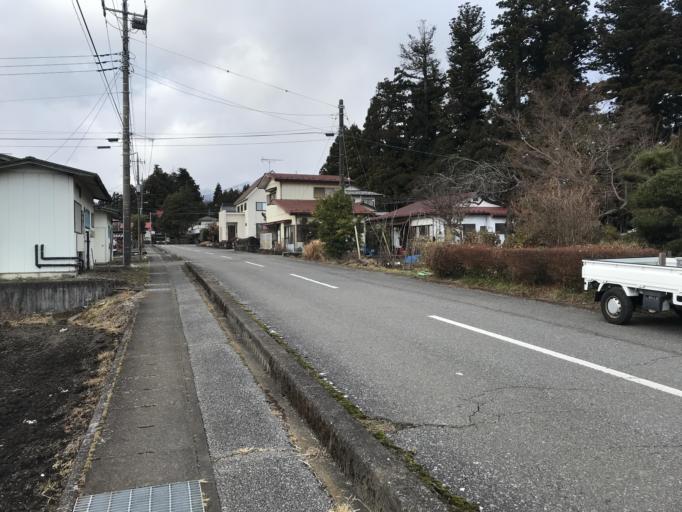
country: JP
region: Tochigi
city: Imaichi
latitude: 36.7281
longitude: 139.6735
